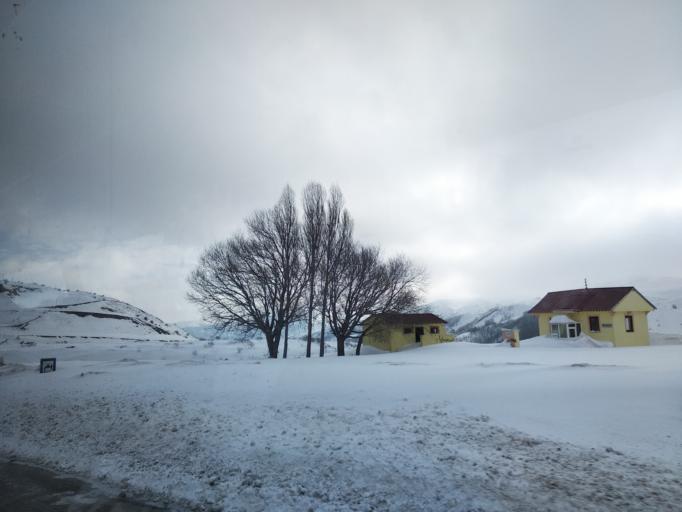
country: TR
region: Erzincan
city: Catalarmut
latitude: 39.8933
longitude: 39.3705
